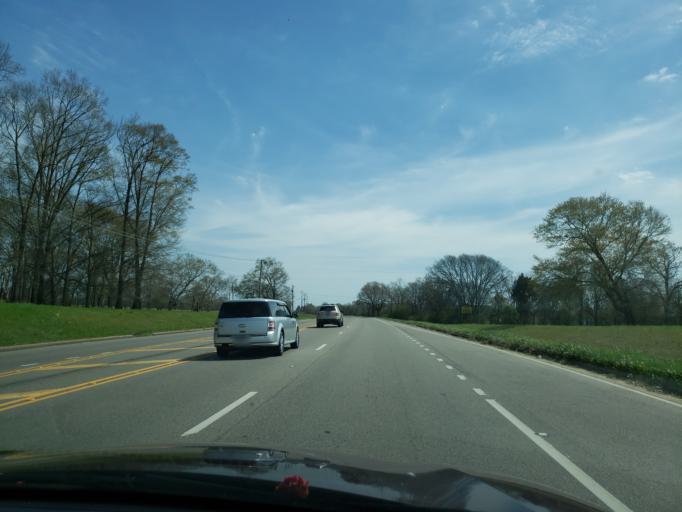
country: US
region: Alabama
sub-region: Autauga County
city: Prattville
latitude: 32.4308
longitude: -86.5524
